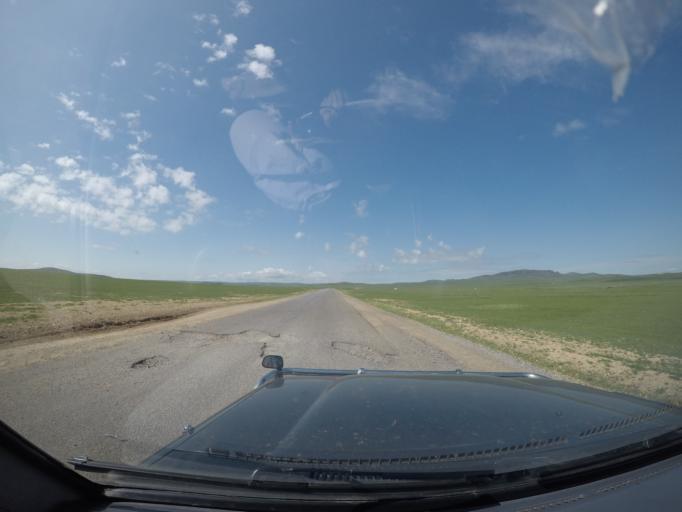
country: MN
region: Hentiy
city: Dundburd
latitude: 47.3423
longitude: 111.4811
